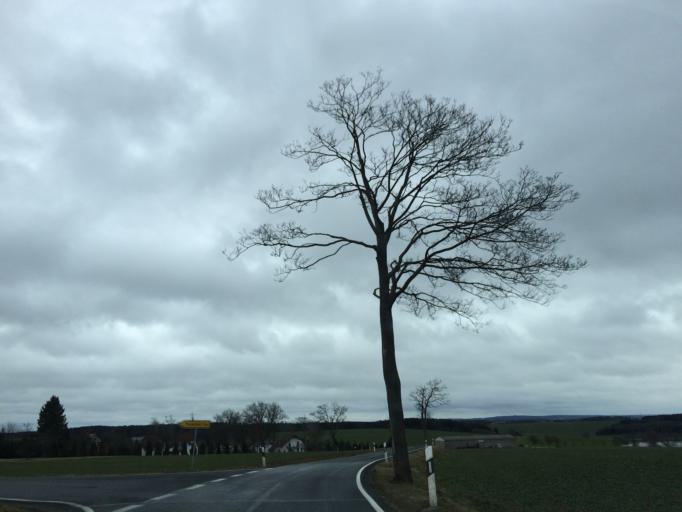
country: DE
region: Thuringia
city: Moxa
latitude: 50.6555
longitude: 11.6354
